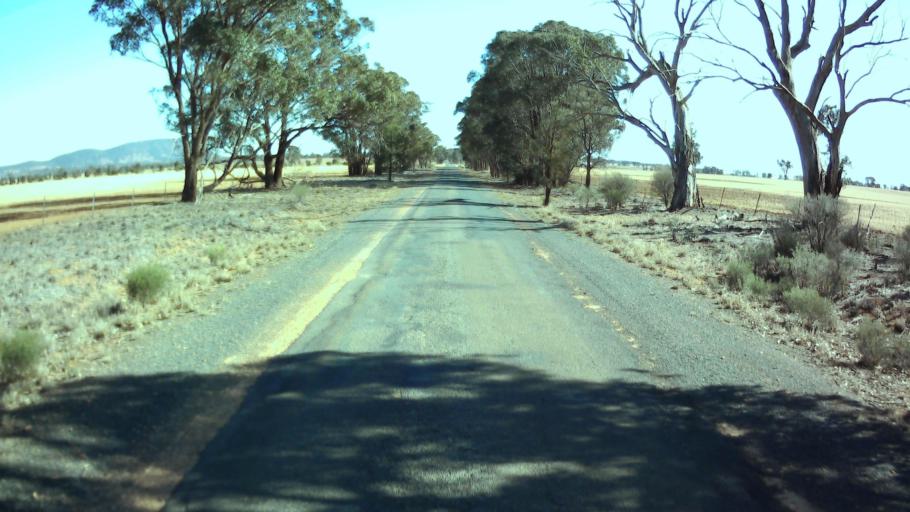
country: AU
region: New South Wales
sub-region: Weddin
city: Grenfell
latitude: -33.8030
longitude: 147.9554
